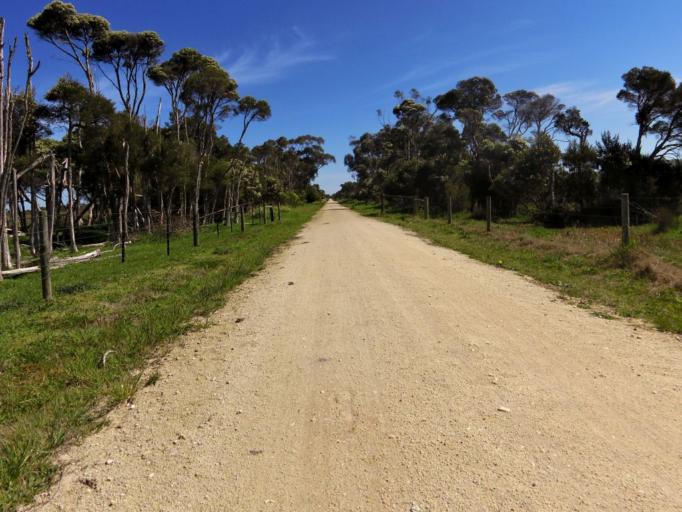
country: AU
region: Victoria
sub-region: Latrobe
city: Morwell
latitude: -38.6683
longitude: 146.4270
